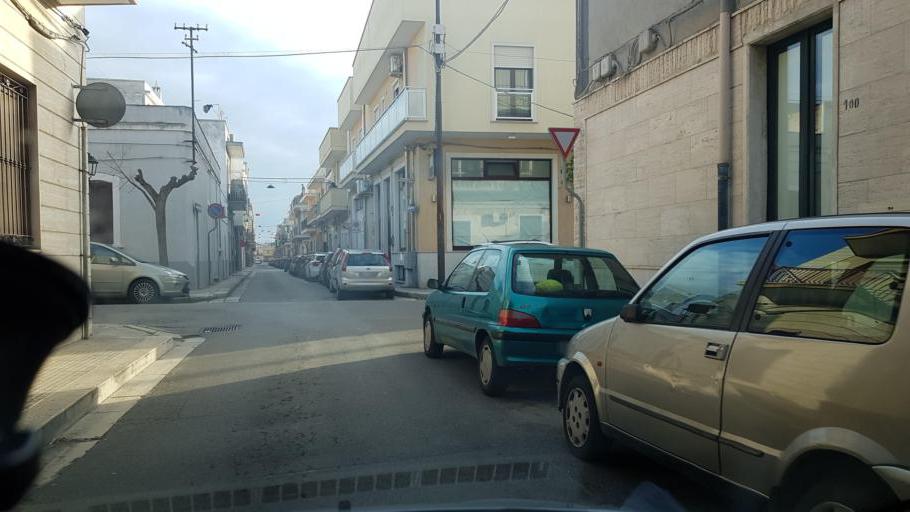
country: IT
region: Apulia
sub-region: Provincia di Brindisi
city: Francavilla Fontana
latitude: 40.5290
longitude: 17.5788
